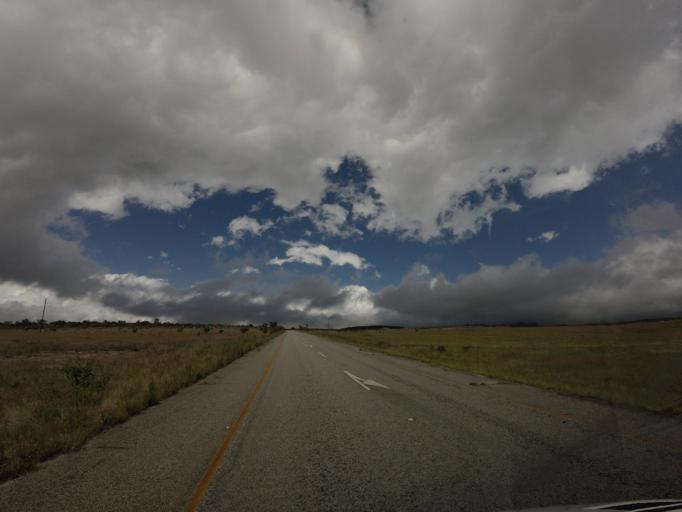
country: ZA
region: Mpumalanga
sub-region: Ehlanzeni District
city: Graksop
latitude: -24.8634
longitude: 30.8593
